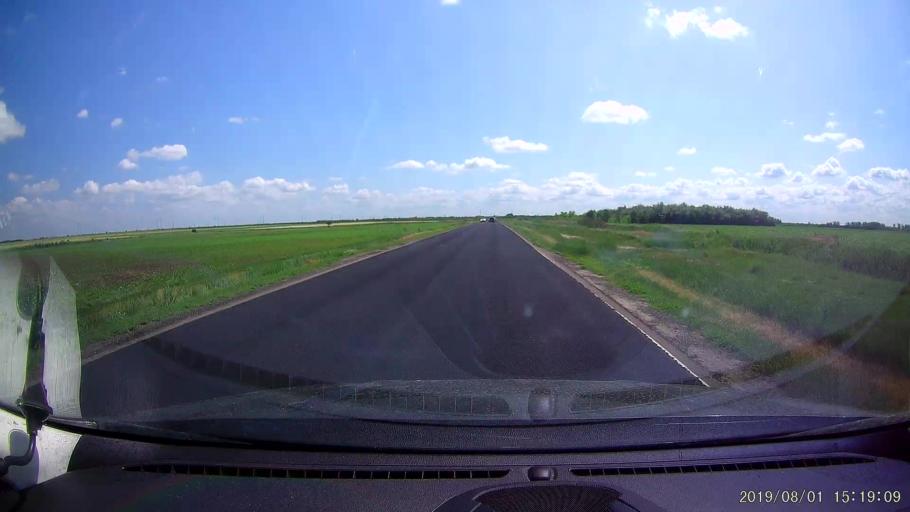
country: RO
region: Braila
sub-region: Comuna Unirea
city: Unirea
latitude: 45.0941
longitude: 27.8149
